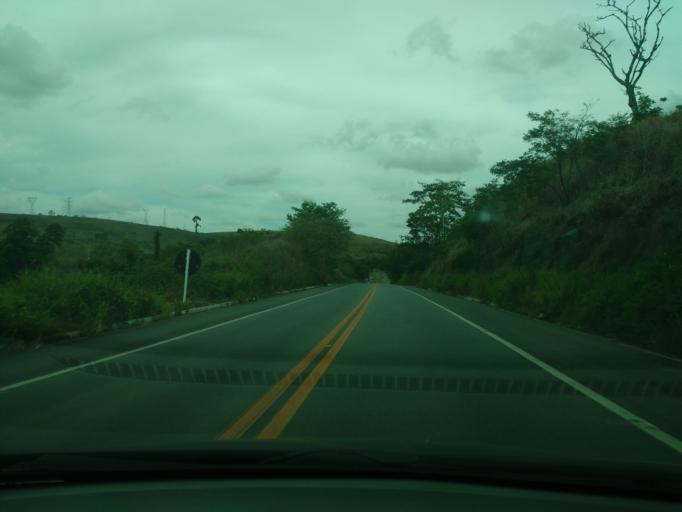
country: BR
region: Alagoas
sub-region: Murici
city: Murici
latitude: -9.2795
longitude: -35.9647
